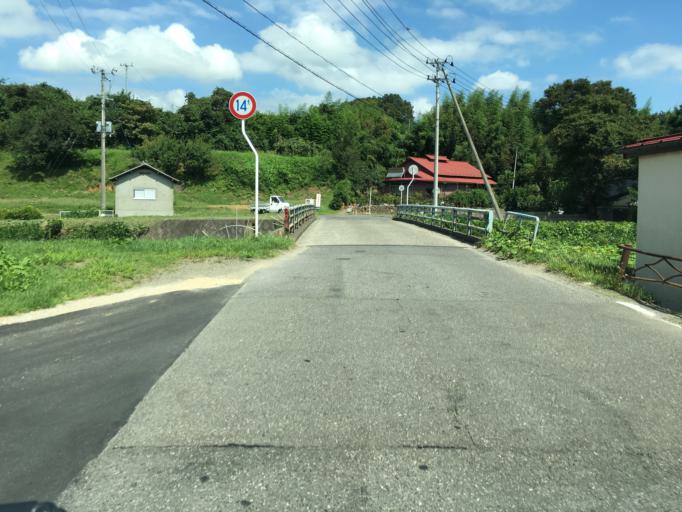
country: JP
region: Fukushima
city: Motomiya
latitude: 37.5193
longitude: 140.3850
